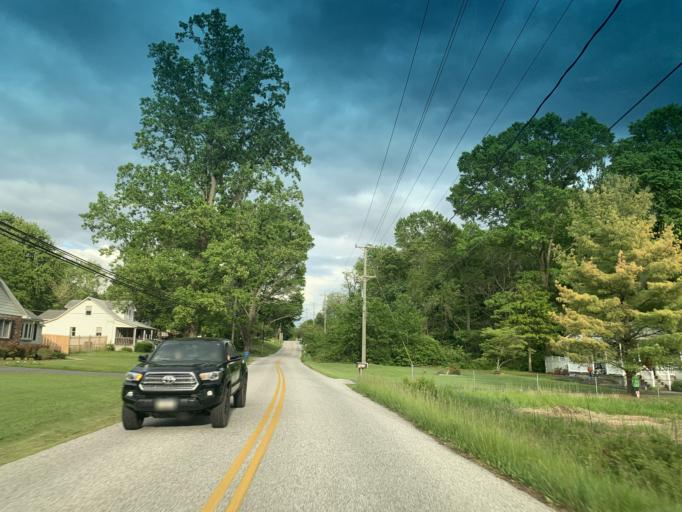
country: US
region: Maryland
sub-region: Harford County
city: South Bel Air
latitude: 39.6552
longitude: -76.2688
